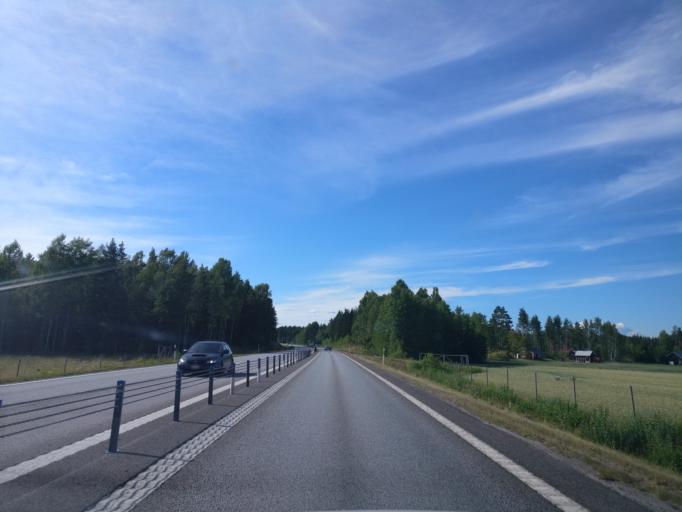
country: SE
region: Vaermland
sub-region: Kils Kommun
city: Kil
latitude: 59.4829
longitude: 13.3523
